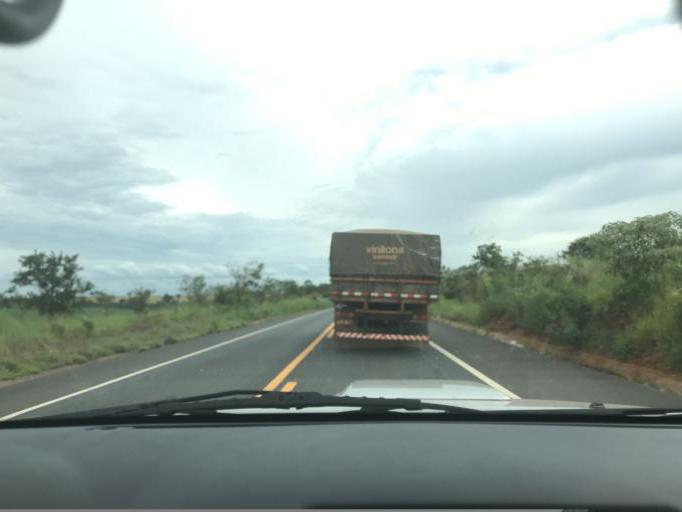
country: BR
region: Minas Gerais
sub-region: Araxa
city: Araxa
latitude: -19.3701
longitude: -46.8557
